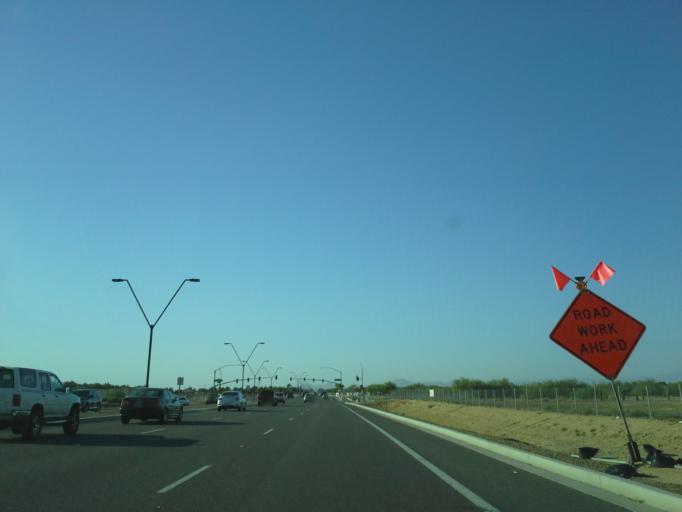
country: US
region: Arizona
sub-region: Maricopa County
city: Queen Creek
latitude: 33.2174
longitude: -111.6344
